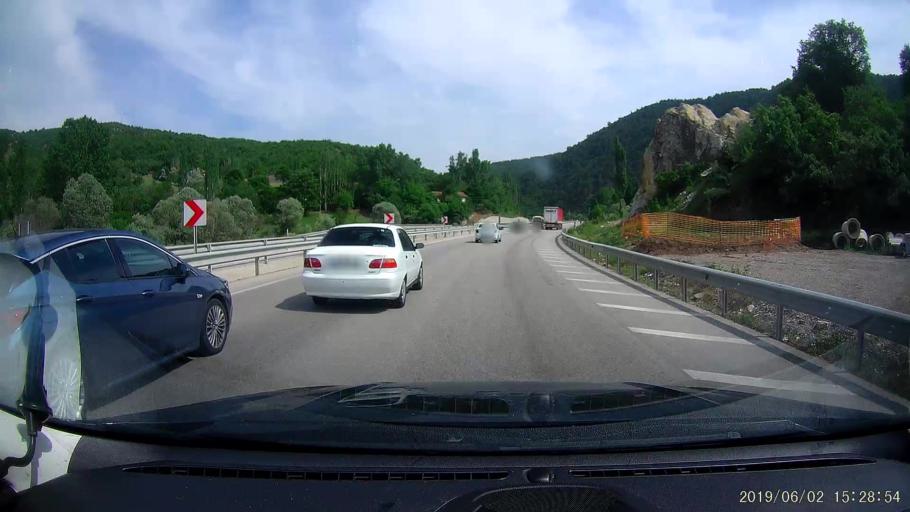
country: TR
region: Amasya
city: Saraycik
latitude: 40.9734
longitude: 35.0824
